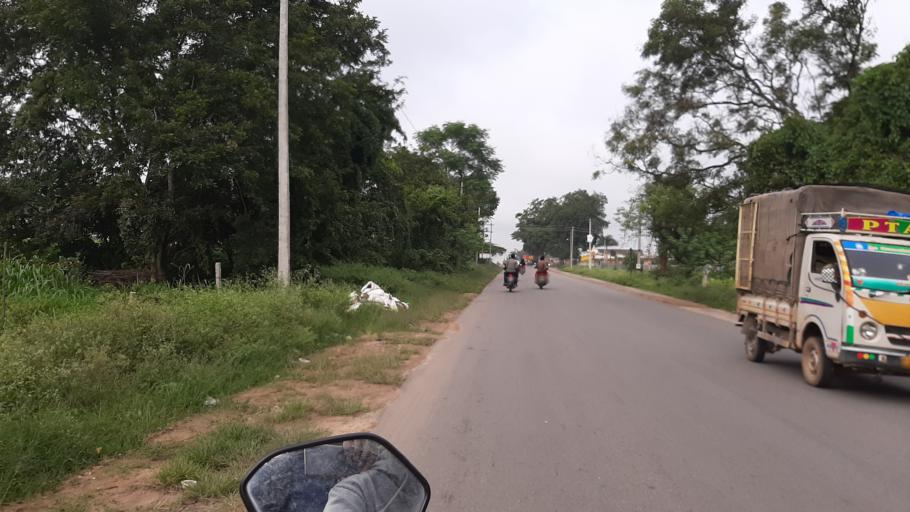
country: IN
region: Karnataka
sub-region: Bangalore Rural
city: Nelamangala
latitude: 12.9699
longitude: 77.4118
